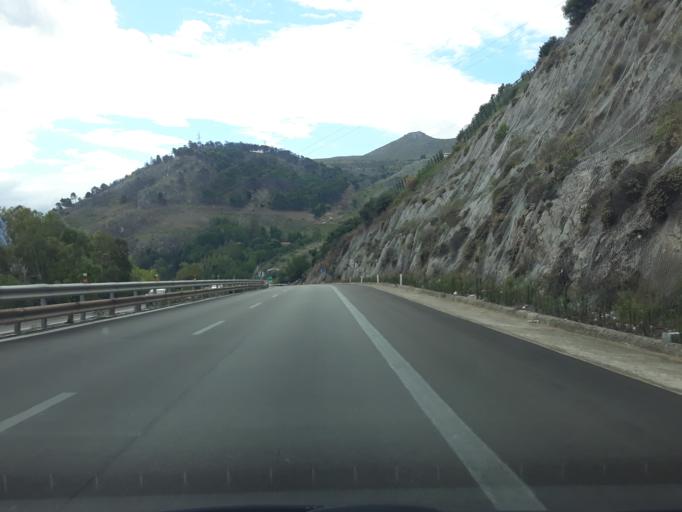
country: IT
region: Sicily
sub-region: Palermo
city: Trabia
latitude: 37.9890
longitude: 13.6549
